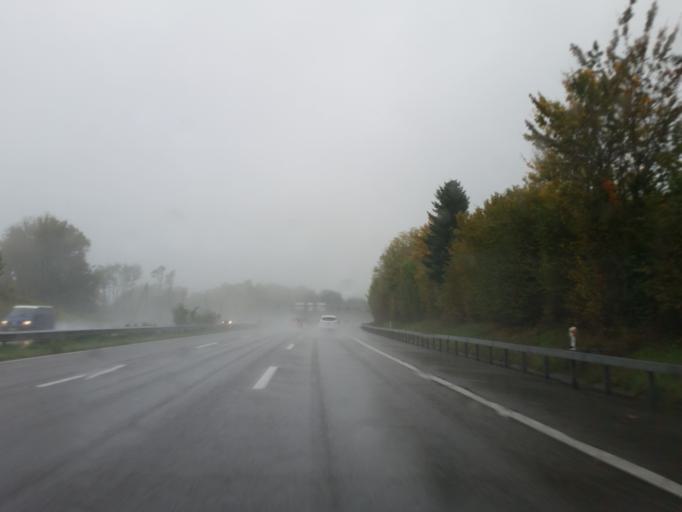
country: CH
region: Saint Gallen
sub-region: Wahlkreis Rorschach
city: Morschwil
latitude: 47.4587
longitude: 9.4342
